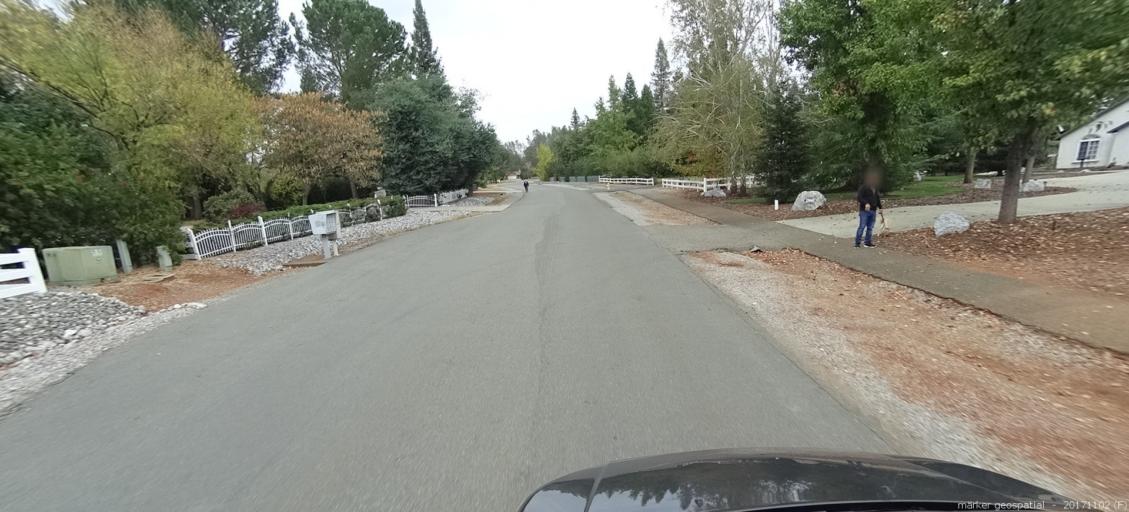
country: US
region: California
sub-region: Shasta County
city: Shasta Lake
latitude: 40.6557
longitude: -122.3225
